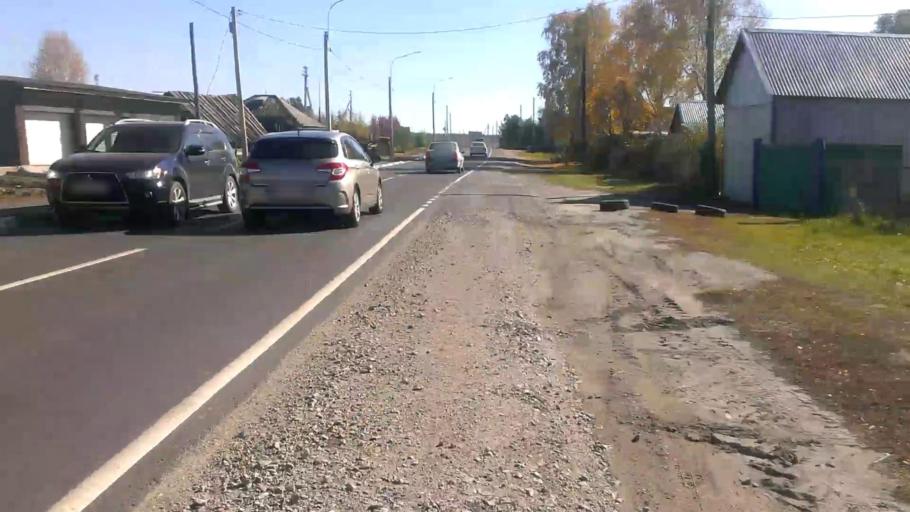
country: RU
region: Altai Krai
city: Sannikovo
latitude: 53.3158
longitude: 83.9589
